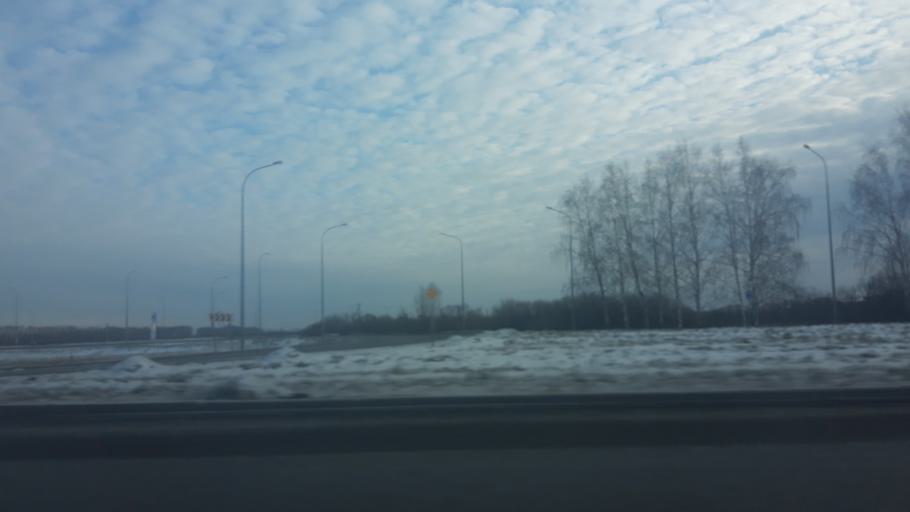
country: RU
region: Tjumen
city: Moskovskiy
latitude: 57.1861
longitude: 65.3570
